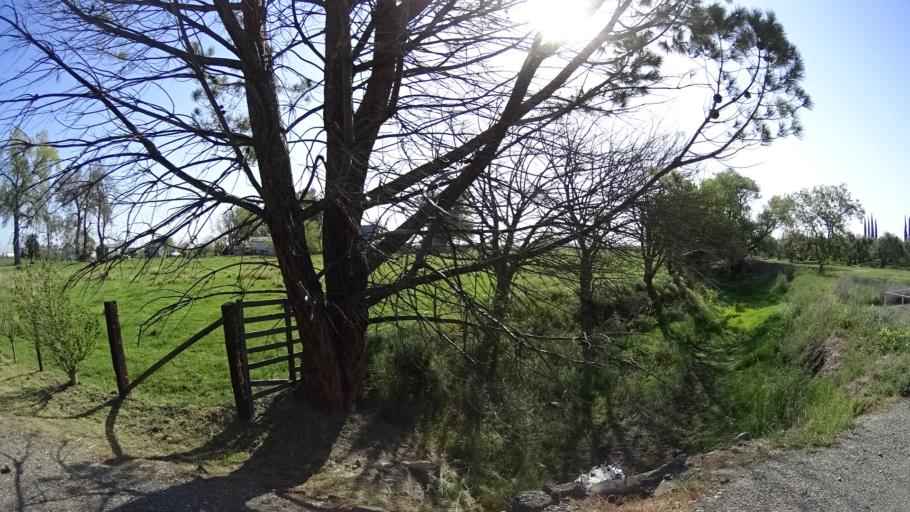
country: US
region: California
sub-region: Glenn County
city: Willows
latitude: 39.5625
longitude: -122.1077
